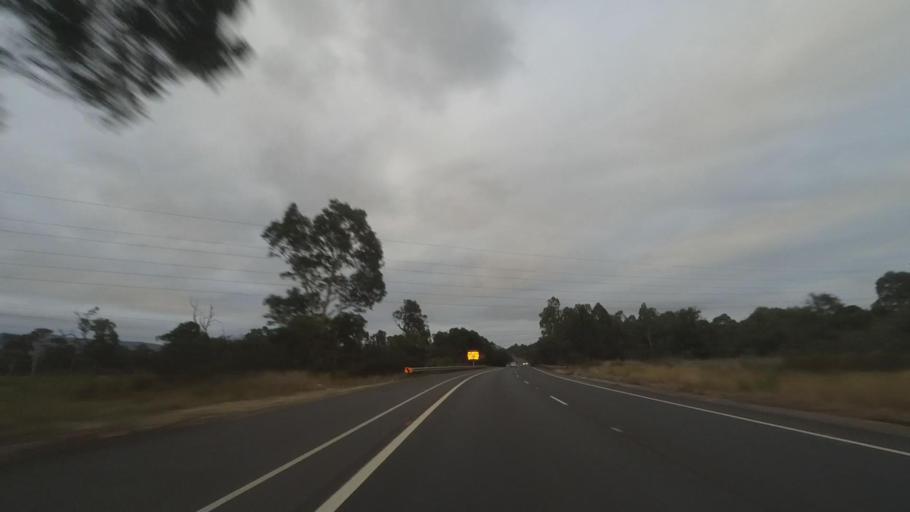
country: AU
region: New South Wales
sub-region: Wollongong
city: Dapto
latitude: -34.5309
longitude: 150.7859
